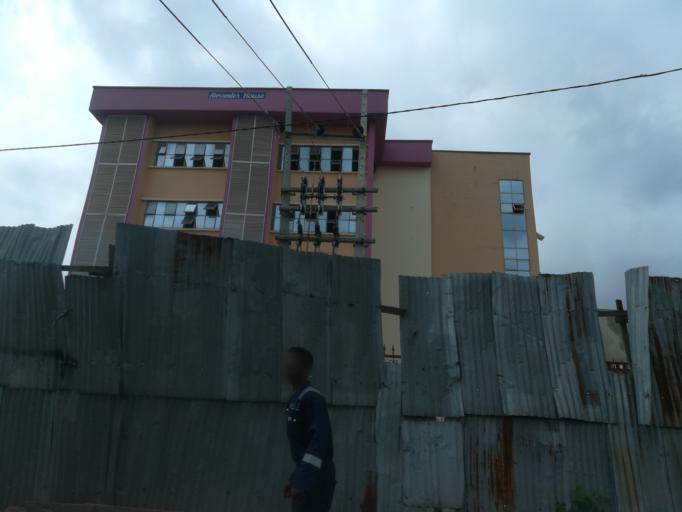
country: NG
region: Lagos
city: Ikeja
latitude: 6.6268
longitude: 3.3632
